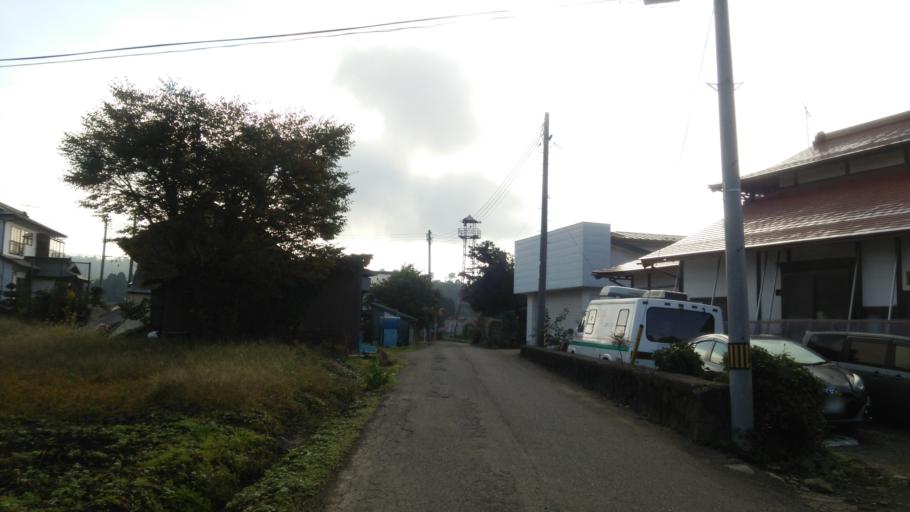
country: JP
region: Fukushima
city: Kitakata
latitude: 37.5403
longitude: 139.9394
